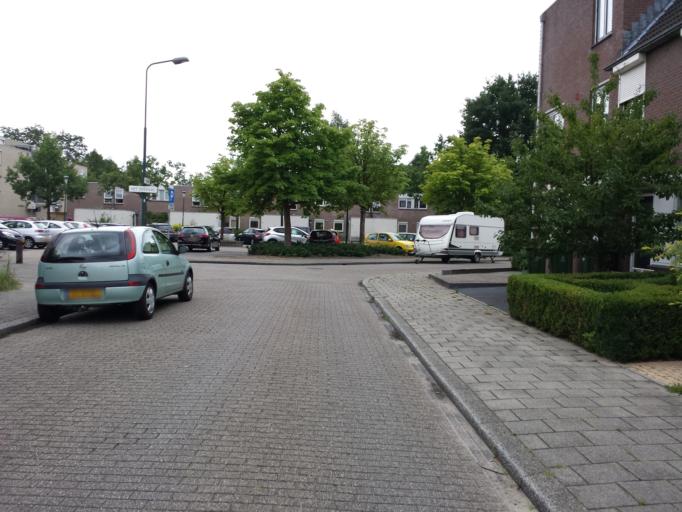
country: NL
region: Utrecht
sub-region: Gemeente Veenendaal
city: Veenendaal
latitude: 52.0294
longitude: 5.5311
